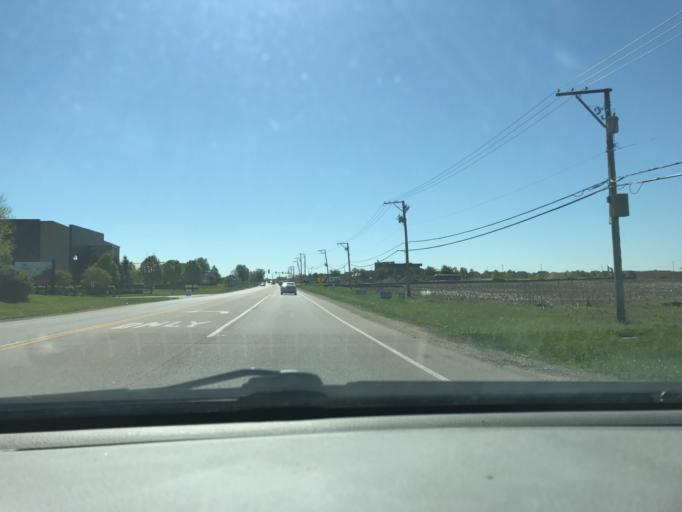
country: US
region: Illinois
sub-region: Kane County
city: Pingree Grove
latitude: 42.0405
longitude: -88.3669
